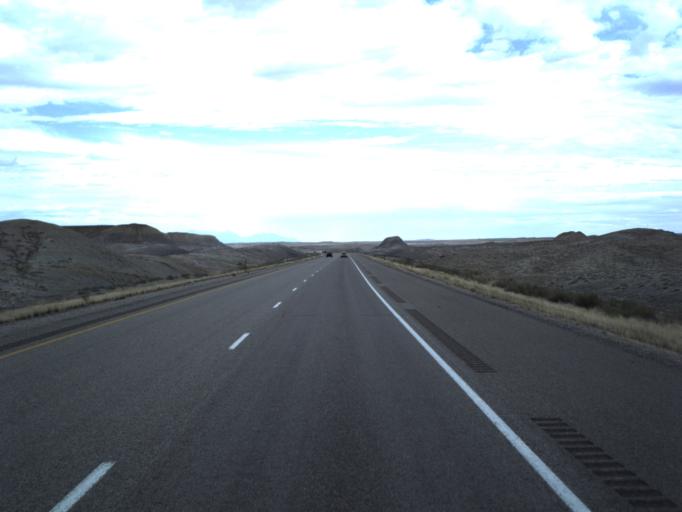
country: US
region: Utah
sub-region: Grand County
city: Moab
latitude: 38.9436
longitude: -110.0379
